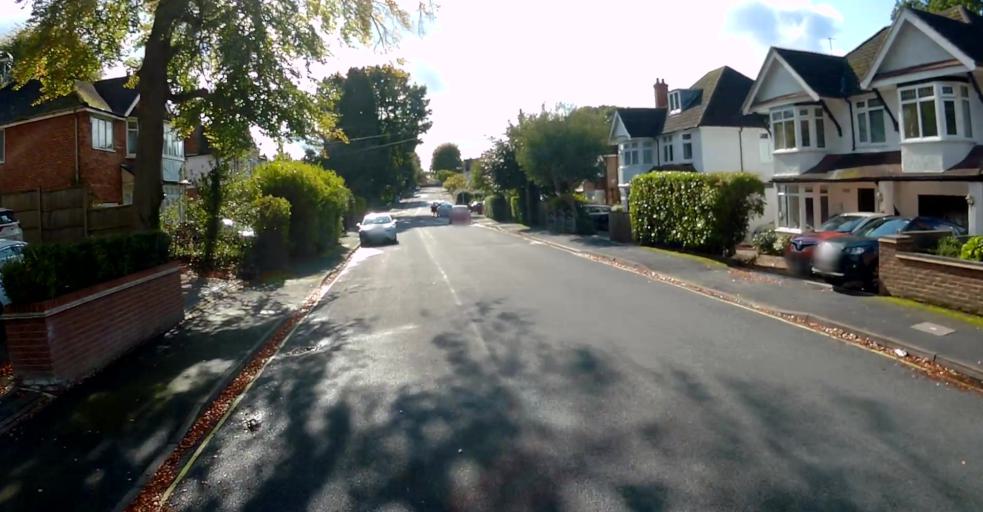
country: GB
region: England
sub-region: Hampshire
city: Farnborough
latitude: 51.2897
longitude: -0.7511
